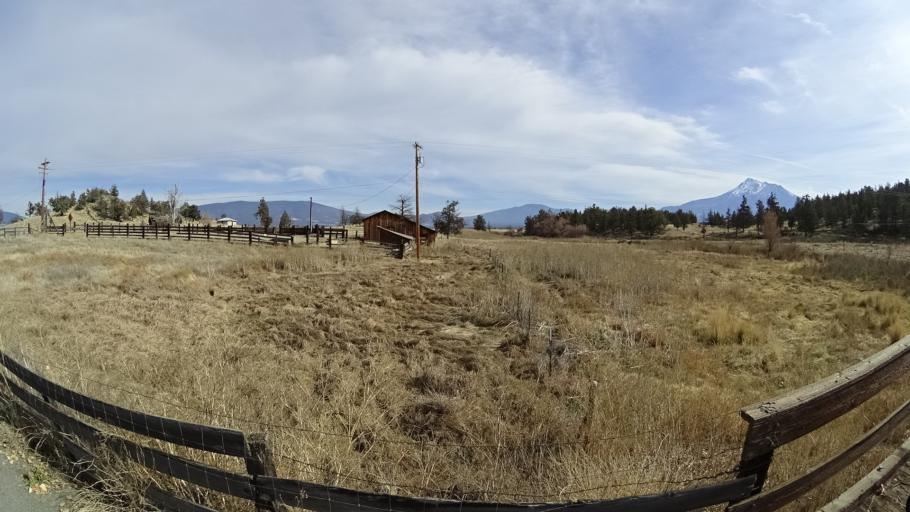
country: US
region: California
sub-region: Siskiyou County
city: Montague
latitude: 41.5910
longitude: -122.4381
